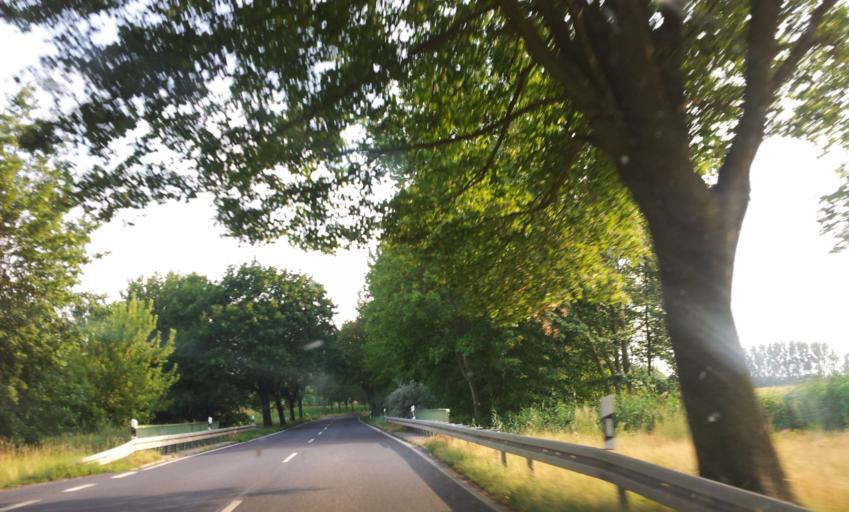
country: DE
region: Brandenburg
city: Treuenbrietzen
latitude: 52.1242
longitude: 12.9822
